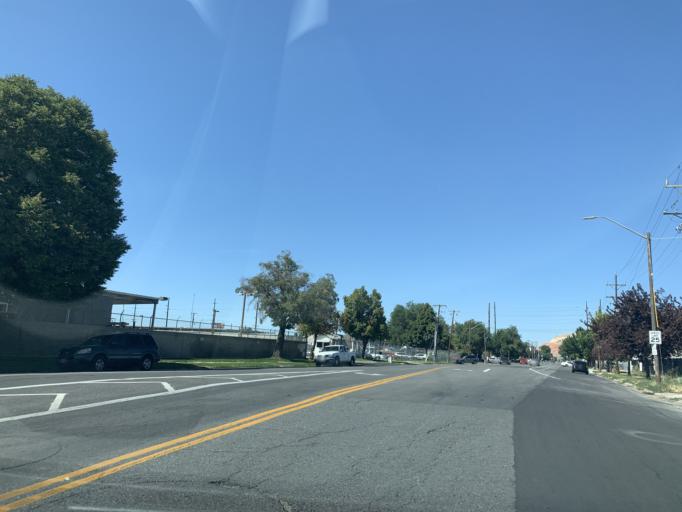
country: US
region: Utah
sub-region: Salt Lake County
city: Salt Lake City
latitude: 40.7653
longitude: -111.9082
